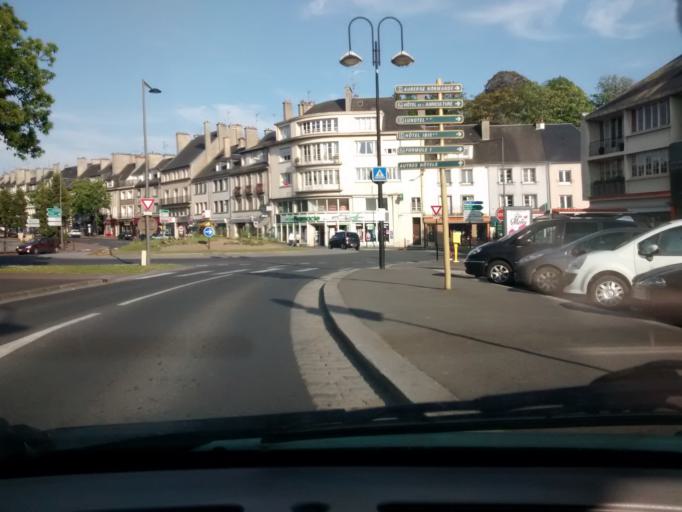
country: FR
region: Lower Normandy
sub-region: Departement de la Manche
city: Agneaux
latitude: 49.1147
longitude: -1.0990
